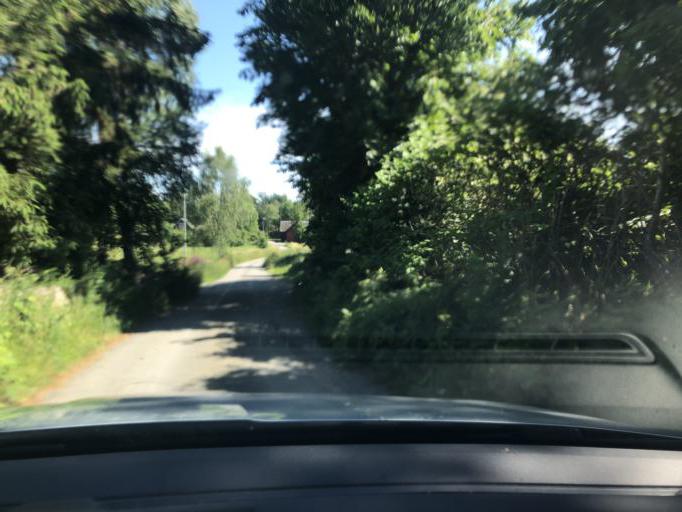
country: SE
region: Blekinge
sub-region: Karlshamns Kommun
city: Morrum
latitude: 56.1827
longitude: 14.7008
